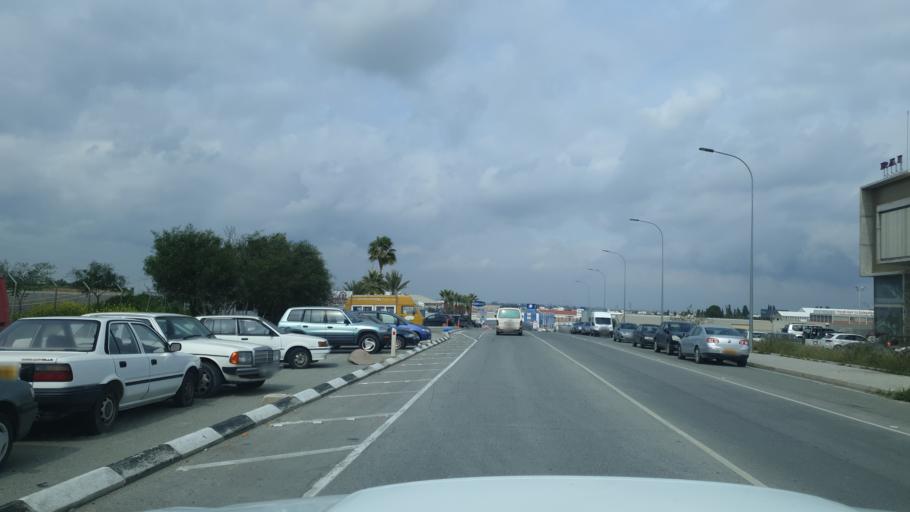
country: CY
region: Lefkosia
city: Geri
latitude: 35.0841
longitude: 33.3807
